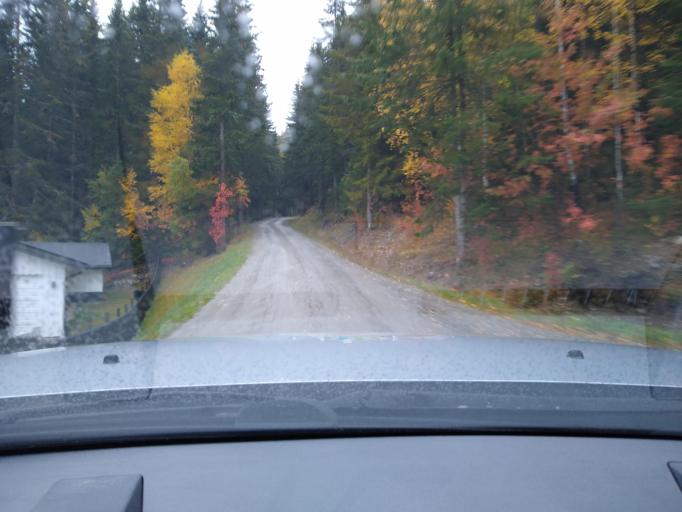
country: NO
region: Oppland
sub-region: Ringebu
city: Ringebu
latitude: 61.5504
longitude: 10.1493
